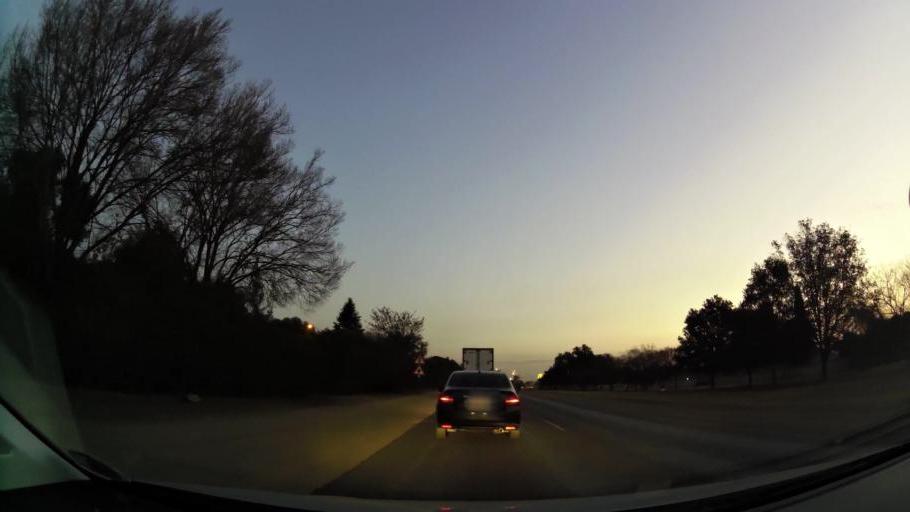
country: ZA
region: Gauteng
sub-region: City of Johannesburg Metropolitan Municipality
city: Modderfontein
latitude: -26.0635
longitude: 28.2230
